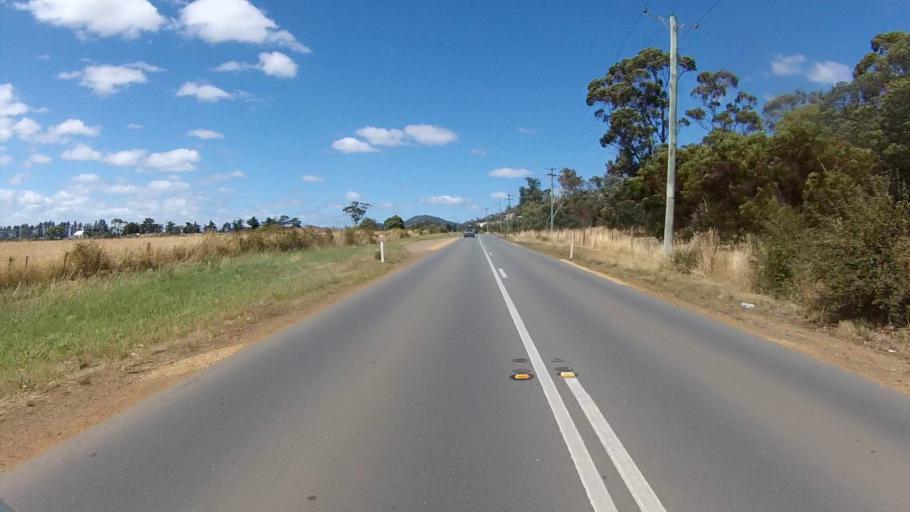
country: AU
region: Tasmania
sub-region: Clarence
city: Cambridge
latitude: -42.7862
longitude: 147.4161
